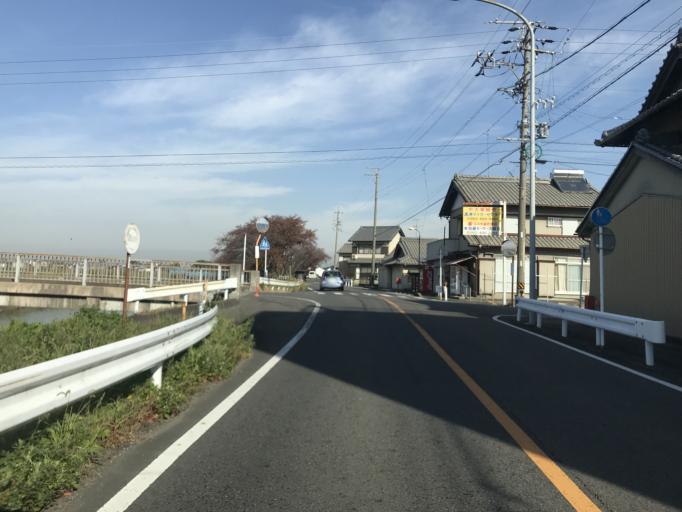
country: JP
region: Aichi
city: Iwakura
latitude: 35.2261
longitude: 136.8463
